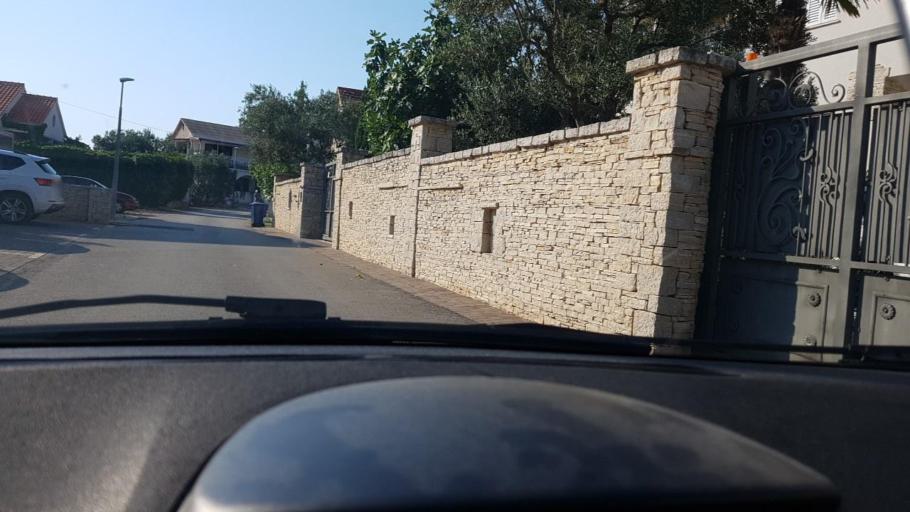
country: HR
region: Sibensko-Kniniska
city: Murter
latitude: 43.8187
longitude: 15.5897
